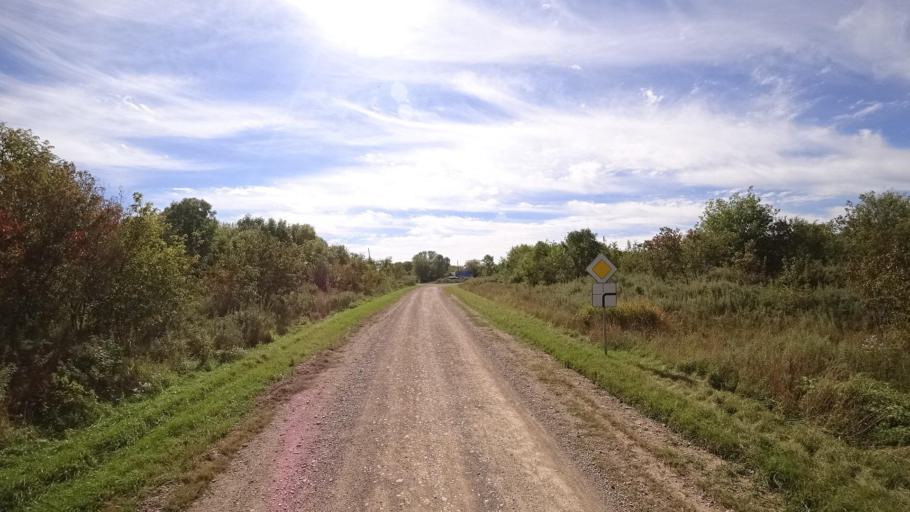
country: RU
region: Primorskiy
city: Kirovskiy
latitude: 44.7602
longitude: 133.6110
